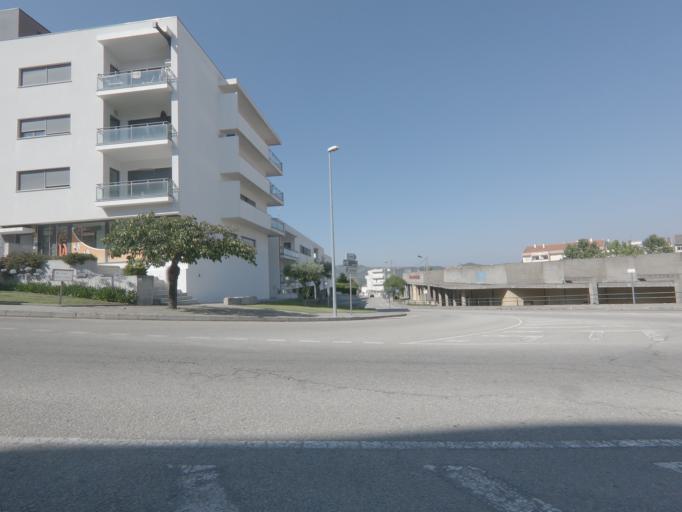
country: PT
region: Viseu
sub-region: Moimenta da Beira
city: Moimenta da Beira
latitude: 40.9778
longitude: -7.6147
